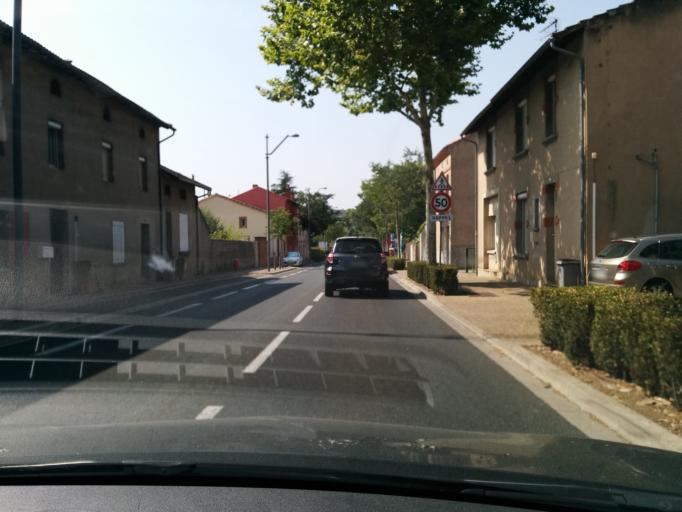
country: FR
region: Midi-Pyrenees
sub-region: Departement du Tarn
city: Albi
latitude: 43.9446
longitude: 2.1338
